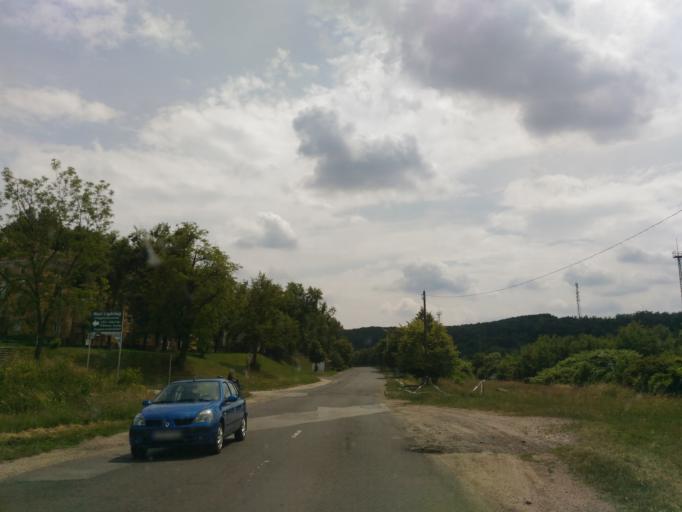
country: HU
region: Baranya
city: Komlo
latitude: 46.1976
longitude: 18.2524
